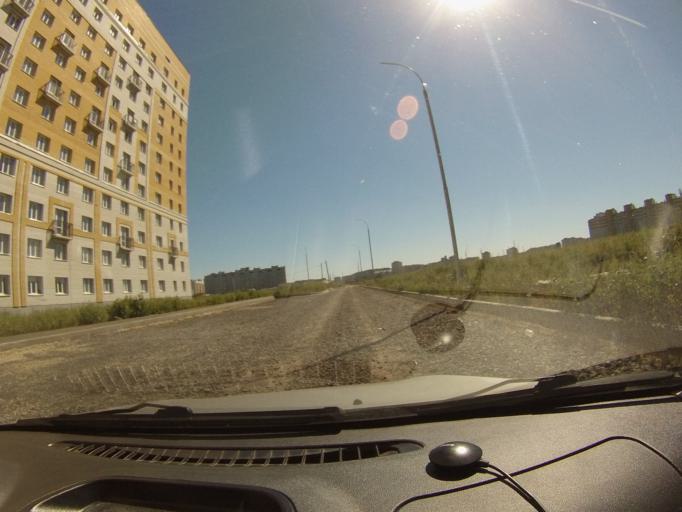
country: RU
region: Tambov
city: Tambov
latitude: 52.7791
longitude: 41.4062
